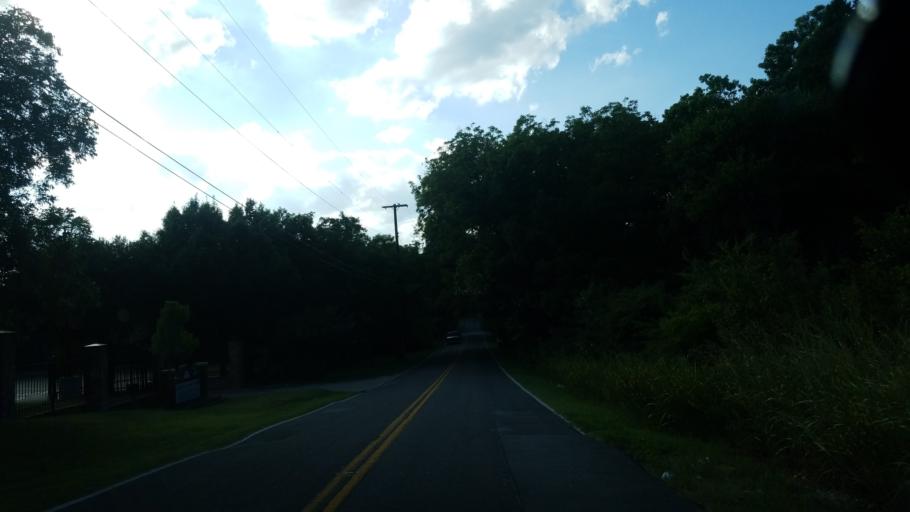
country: US
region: Texas
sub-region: Dallas County
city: Dallas
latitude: 32.7800
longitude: -96.7131
